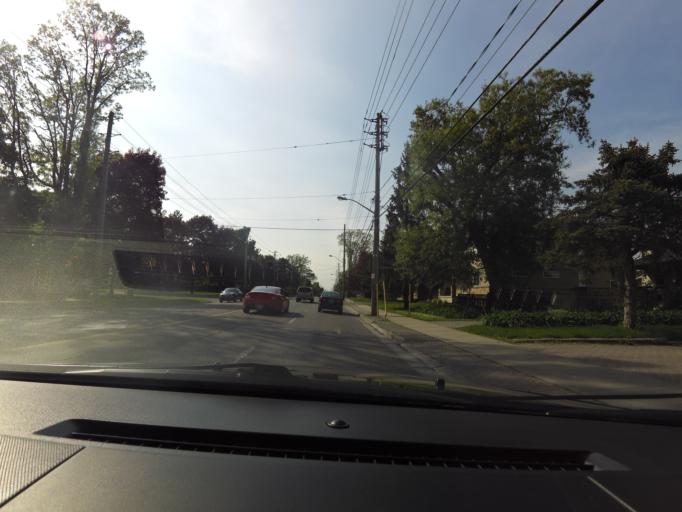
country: CA
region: Ontario
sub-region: Wellington County
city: Guelph
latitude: 43.5257
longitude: -80.2419
